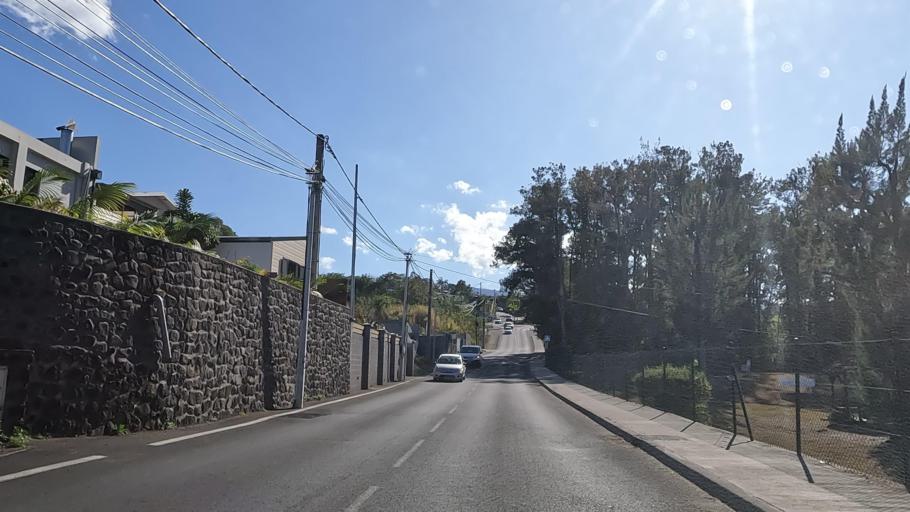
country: RE
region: Reunion
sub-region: Reunion
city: Le Tampon
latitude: -21.2590
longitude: 55.5111
